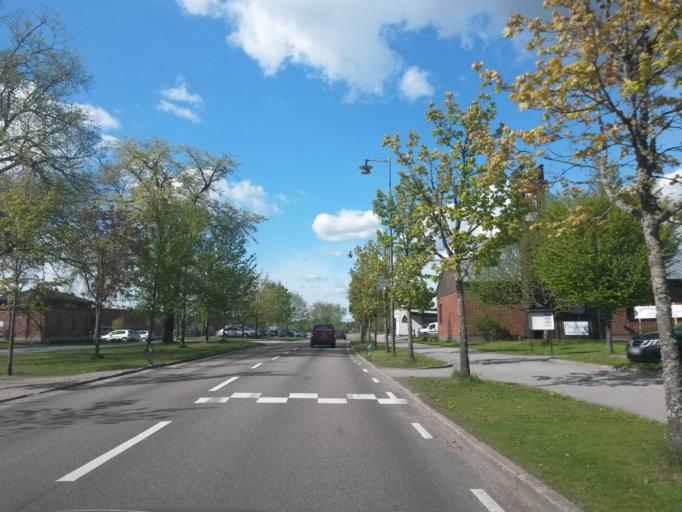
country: SE
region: Vaestra Goetaland
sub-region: Boras Kommun
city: Boras
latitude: 57.8267
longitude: 13.0095
